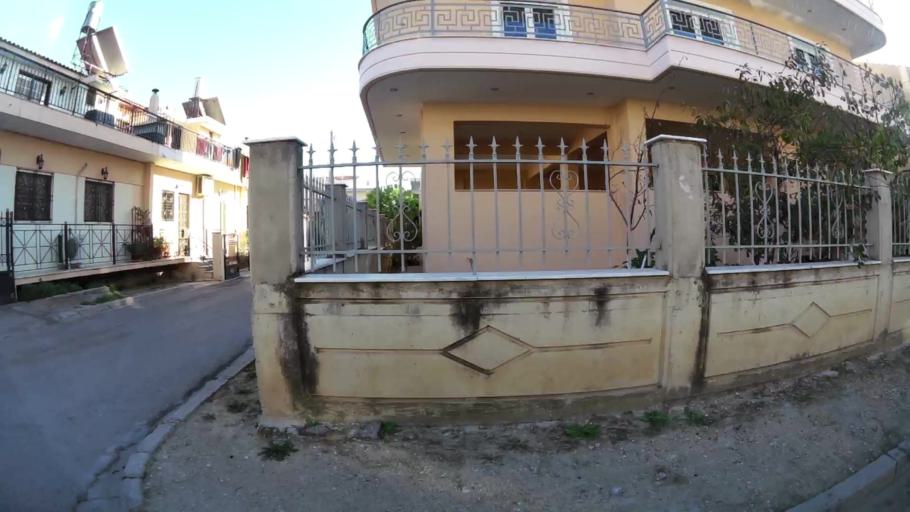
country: GR
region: Attica
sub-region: Nomarchia Anatolikis Attikis
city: Acharnes
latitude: 38.0823
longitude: 23.7288
